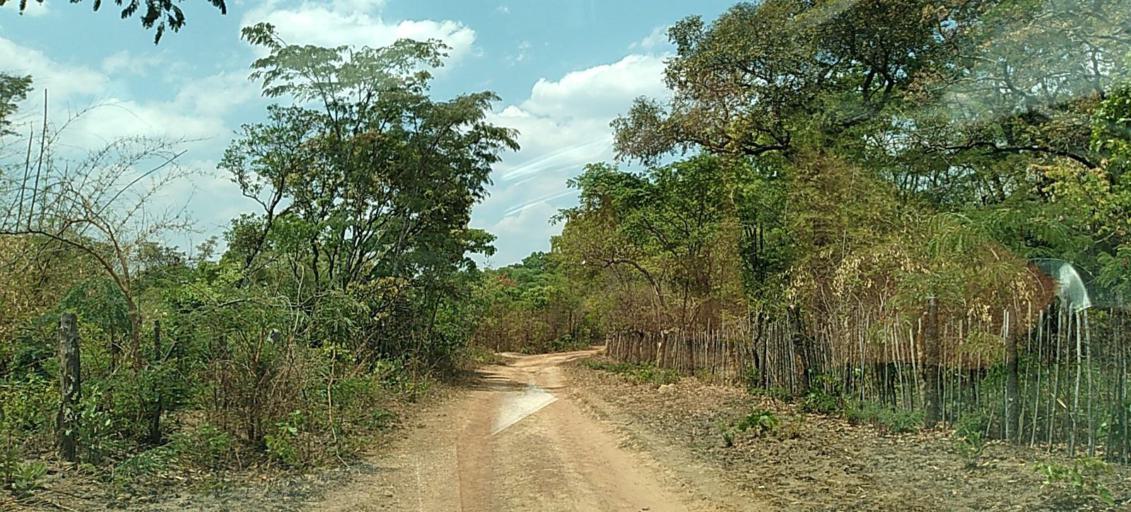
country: ZM
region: Copperbelt
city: Chililabombwe
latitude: -12.4834
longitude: 27.6423
